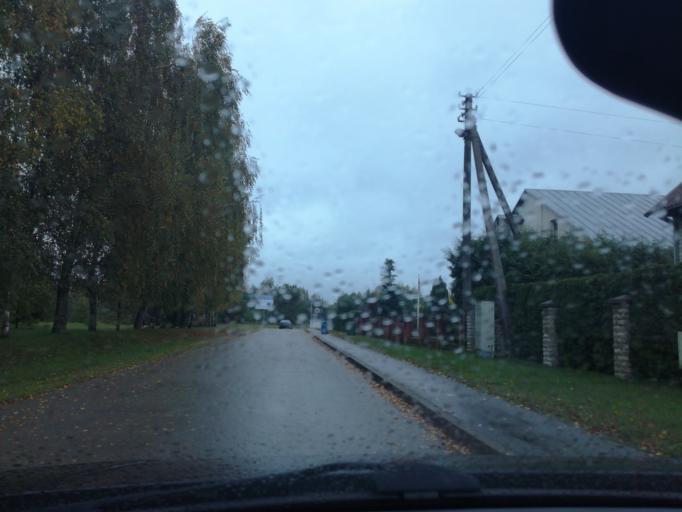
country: LT
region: Alytaus apskritis
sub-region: Alytus
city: Alytus
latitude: 54.4047
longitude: 24.0534
